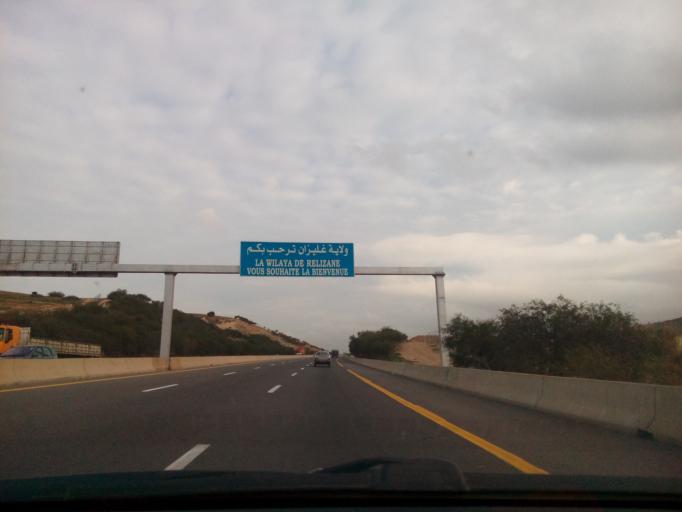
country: DZ
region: Mostaganem
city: Mostaganem
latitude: 35.7056
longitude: 0.2296
